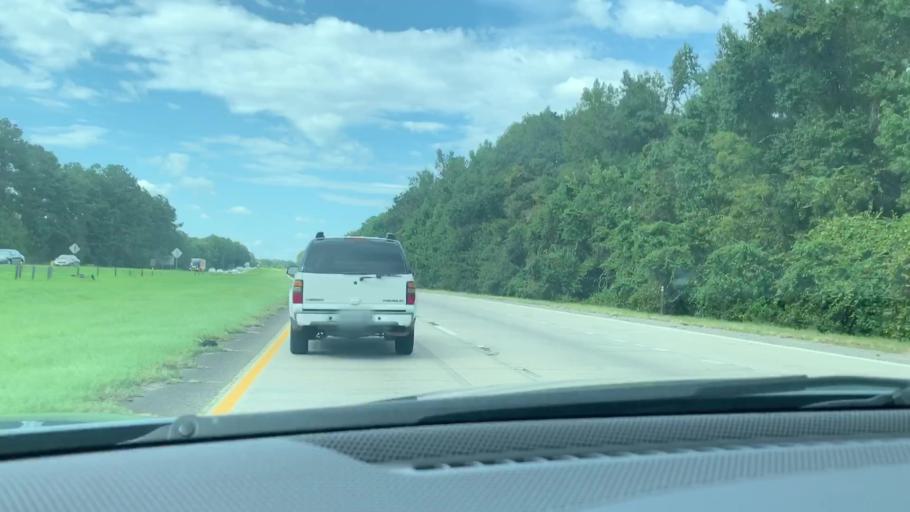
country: US
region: South Carolina
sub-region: Hampton County
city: Yemassee
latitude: 32.6369
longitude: -80.8817
